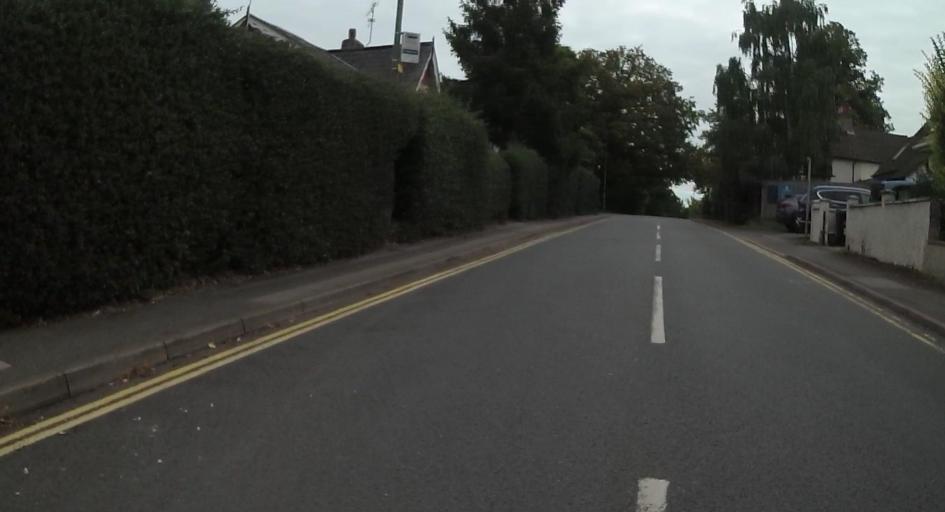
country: GB
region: England
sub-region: Surrey
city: Woking
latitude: 51.3221
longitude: -0.5382
